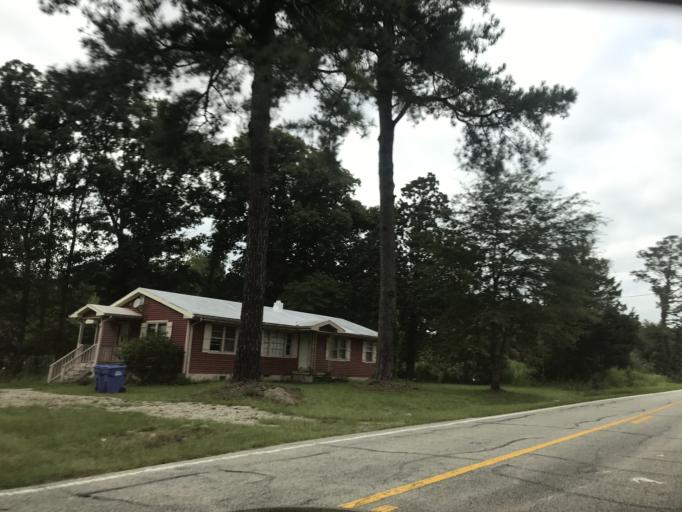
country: US
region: North Carolina
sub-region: Wake County
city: Garner
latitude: 35.5738
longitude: -78.5860
